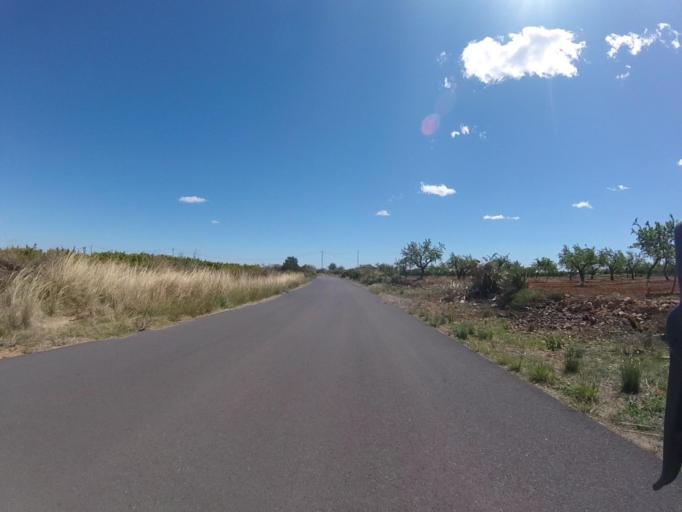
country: ES
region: Valencia
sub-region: Provincia de Castello
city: Orpesa/Oropesa del Mar
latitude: 40.1661
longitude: 0.1550
